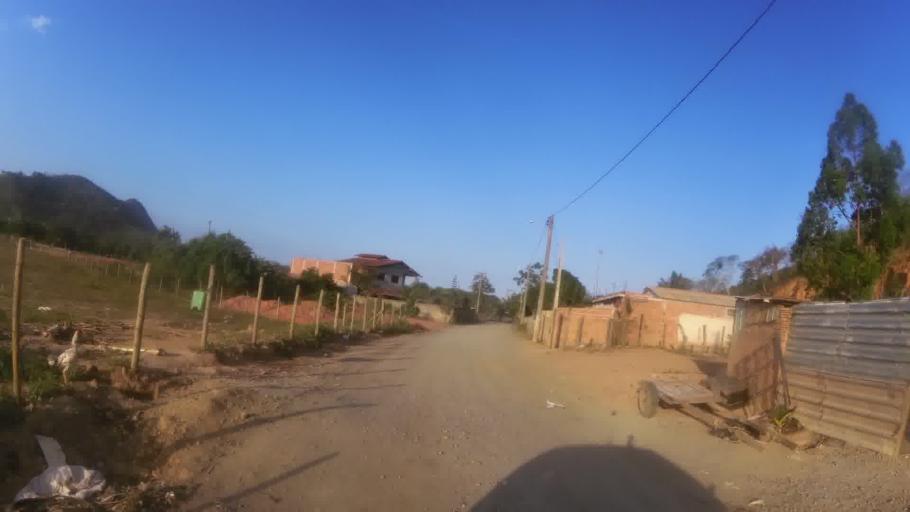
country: BR
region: Espirito Santo
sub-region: Piuma
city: Piuma
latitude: -20.8903
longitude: -40.7875
